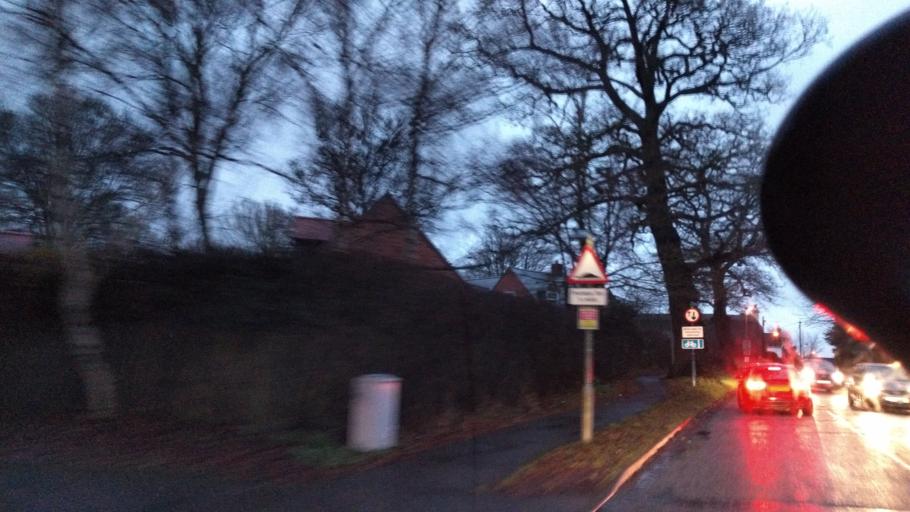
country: GB
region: England
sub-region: Oxfordshire
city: Shrivenham
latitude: 51.6015
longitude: -1.6517
